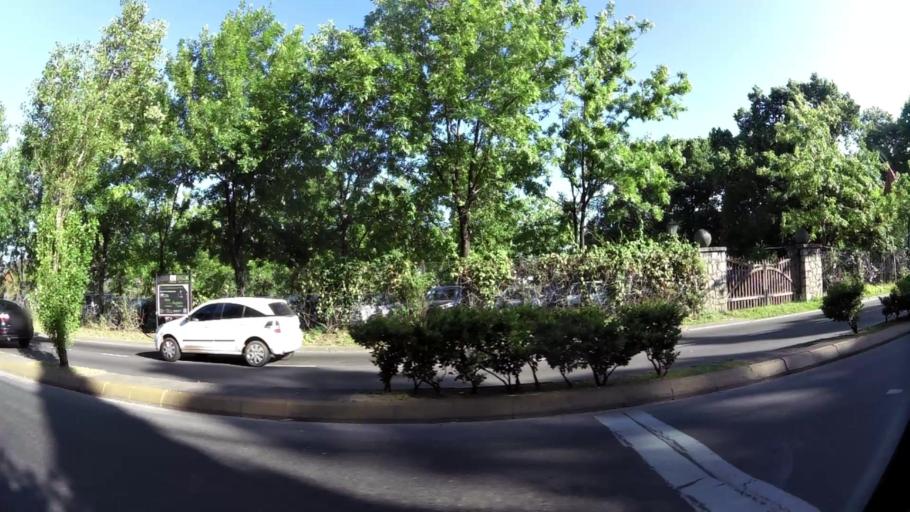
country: AR
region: Buenos Aires
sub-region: Partido de San Isidro
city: San Isidro
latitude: -34.4850
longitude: -58.5332
